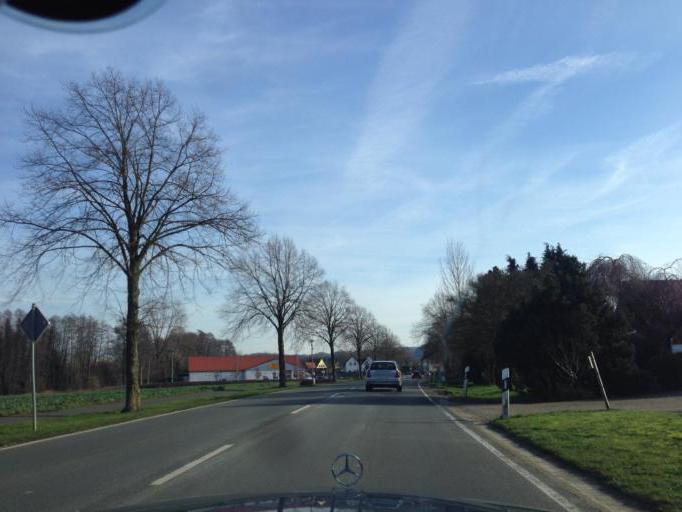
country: DE
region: North Rhine-Westphalia
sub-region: Regierungsbezirk Munster
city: Tecklenburg
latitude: 52.2386
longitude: 7.8180
